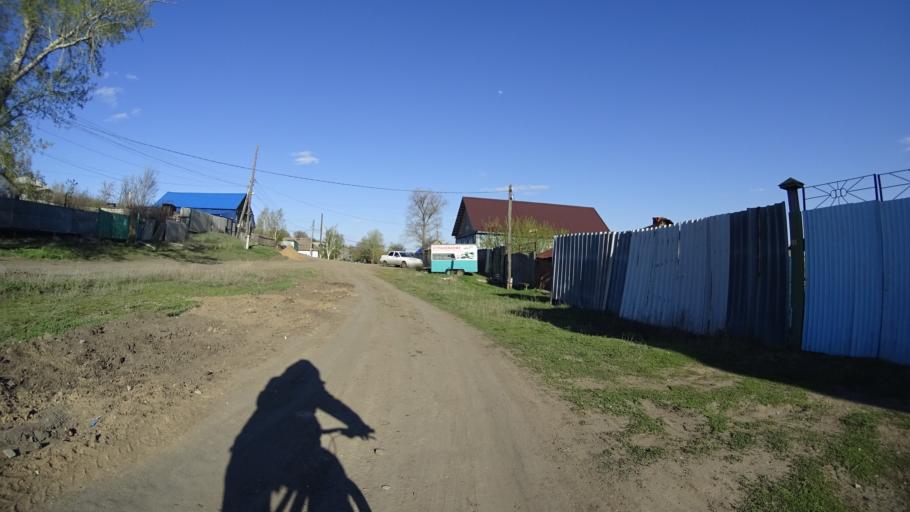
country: RU
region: Chelyabinsk
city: Troitsk
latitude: 54.0984
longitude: 61.5446
